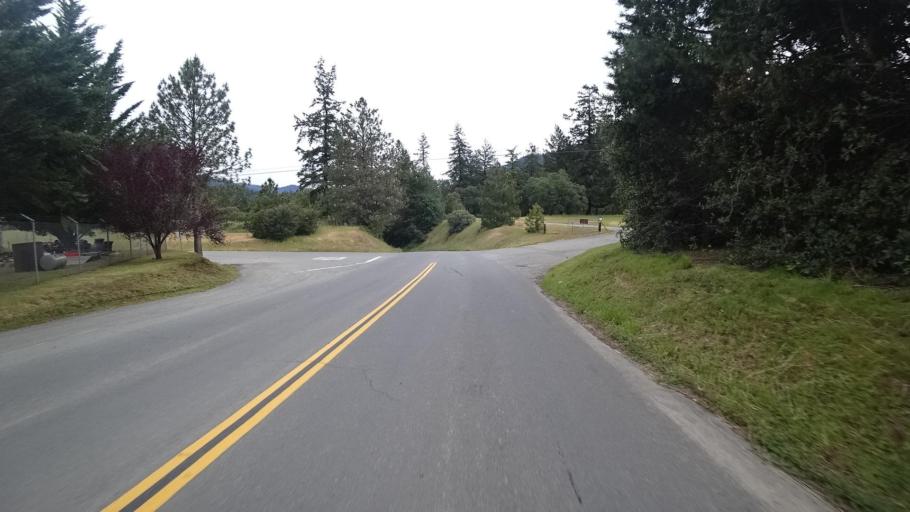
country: US
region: California
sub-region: Humboldt County
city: Willow Creek
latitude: 40.9436
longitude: -123.6227
